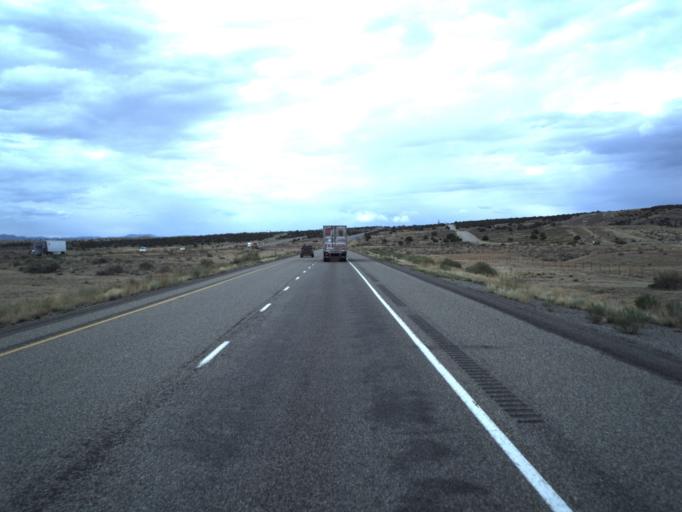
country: US
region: Colorado
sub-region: Mesa County
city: Loma
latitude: 39.1506
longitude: -109.1479
